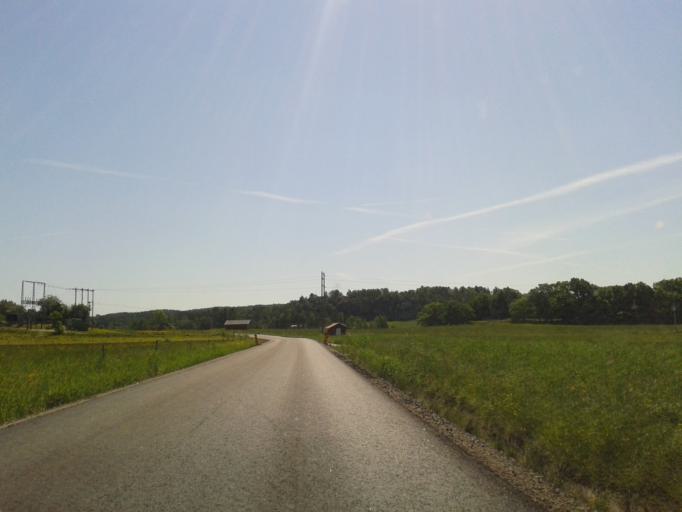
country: SE
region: Vaestra Goetaland
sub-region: Orust
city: Henan
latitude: 58.2585
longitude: 11.7349
